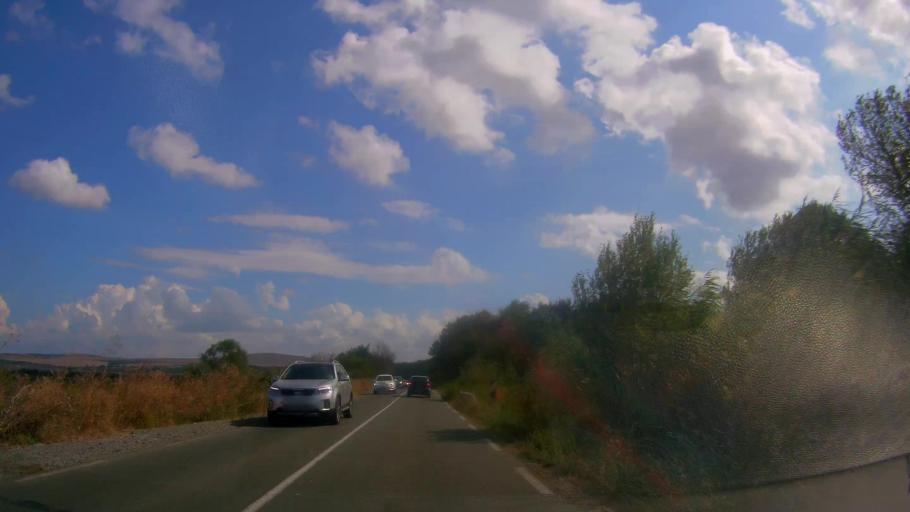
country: BG
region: Burgas
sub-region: Obshtina Kameno
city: Kameno
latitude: 42.4892
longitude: 27.3390
